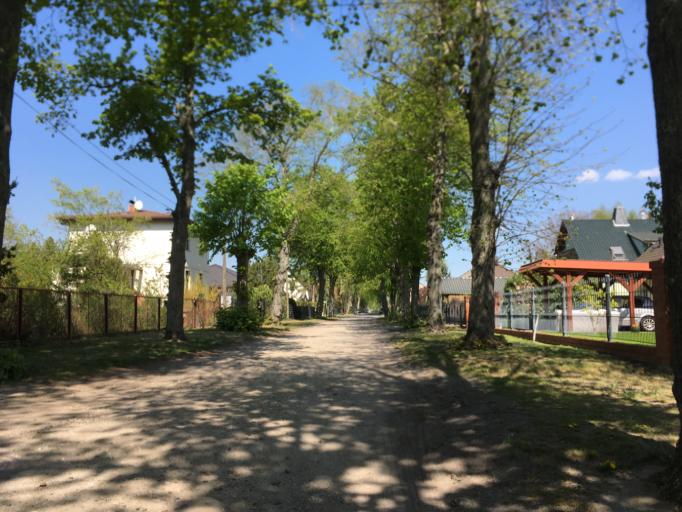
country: DE
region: Berlin
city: Buch
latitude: 52.6690
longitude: 13.5358
